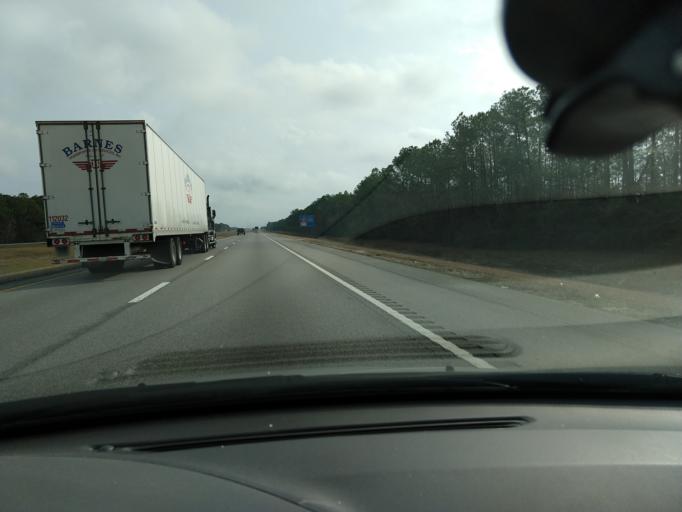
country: US
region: Mississippi
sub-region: Jackson County
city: Hickory Hills
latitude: 30.4326
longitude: -88.6759
